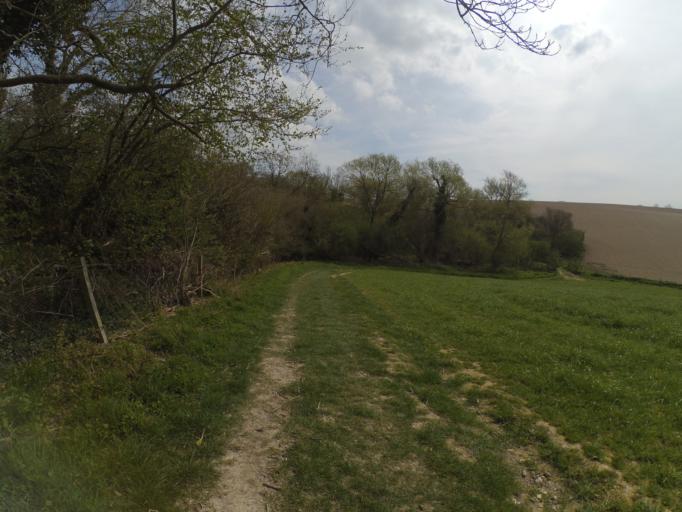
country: GB
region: England
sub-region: West Sussex
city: Arundel
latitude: 50.8800
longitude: -0.5505
